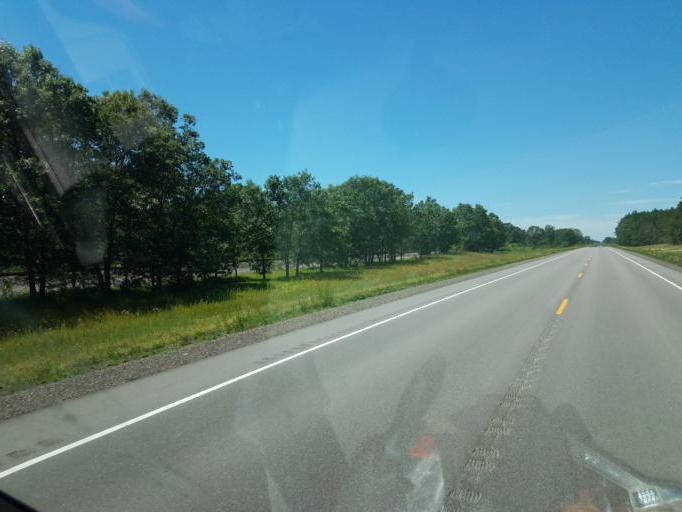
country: US
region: Wisconsin
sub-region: Juneau County
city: New Lisbon
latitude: 44.0249
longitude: -90.1427
